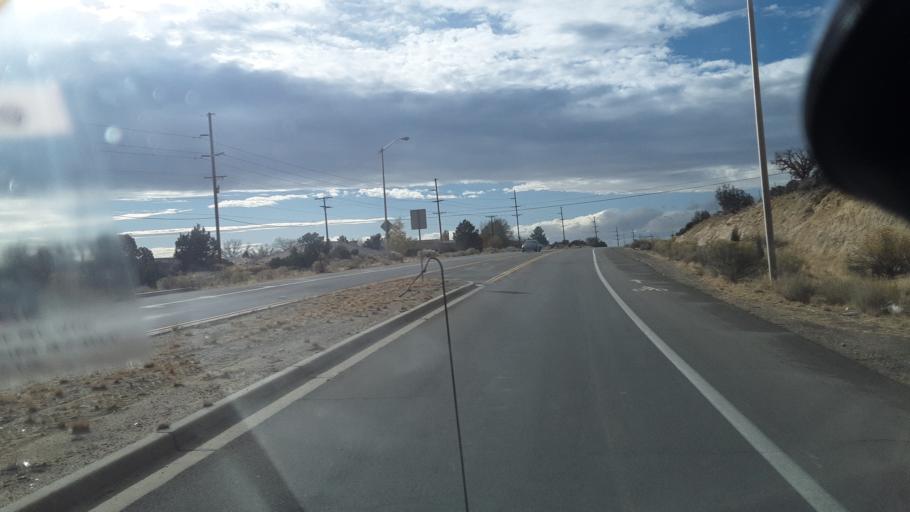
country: US
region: New Mexico
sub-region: San Juan County
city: Farmington
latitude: 36.7739
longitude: -108.1874
